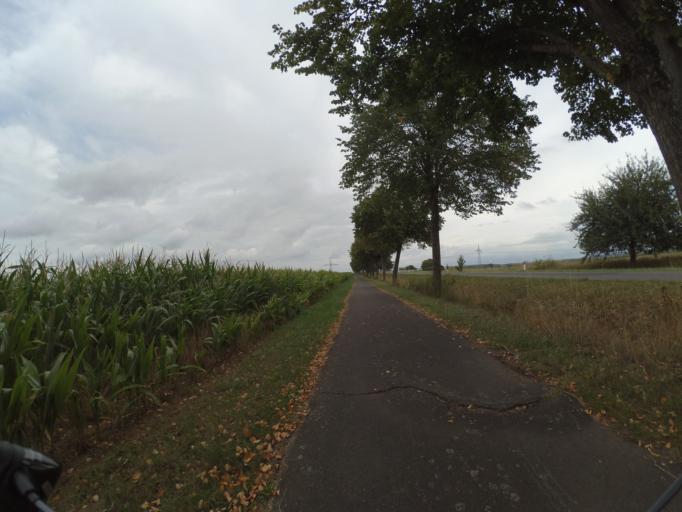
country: DE
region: Rheinland-Pfalz
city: Beilingen
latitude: 49.9443
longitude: 6.6523
